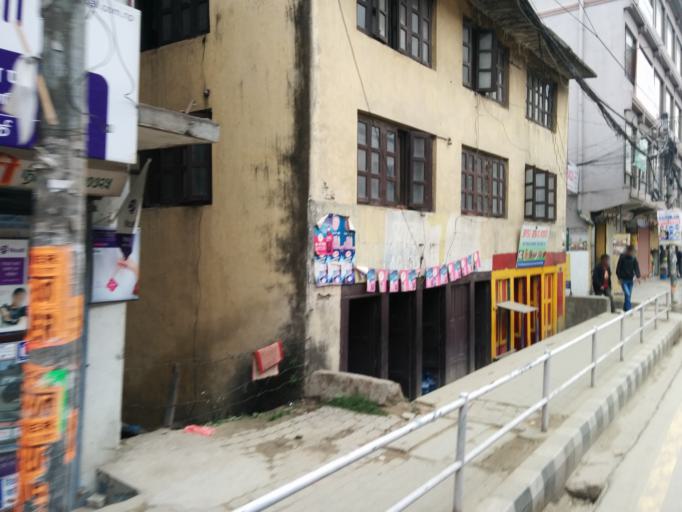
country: NP
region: Central Region
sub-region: Bagmati Zone
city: Kathmandu
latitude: 27.7122
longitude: 85.3450
